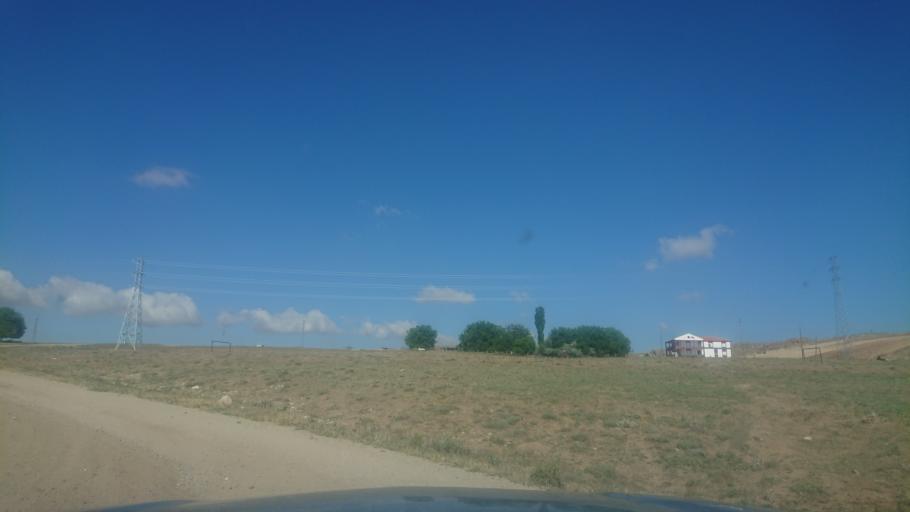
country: TR
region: Aksaray
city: Agacoren
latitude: 38.9193
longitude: 33.9230
